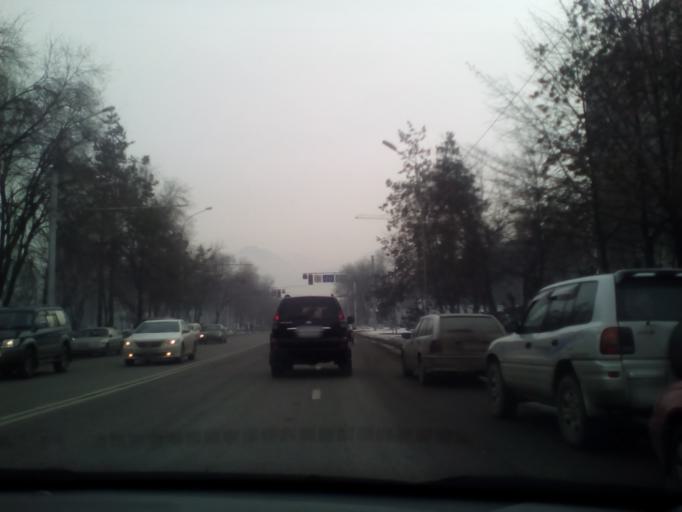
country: KZ
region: Almaty Qalasy
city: Almaty
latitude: 43.2340
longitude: 76.8317
